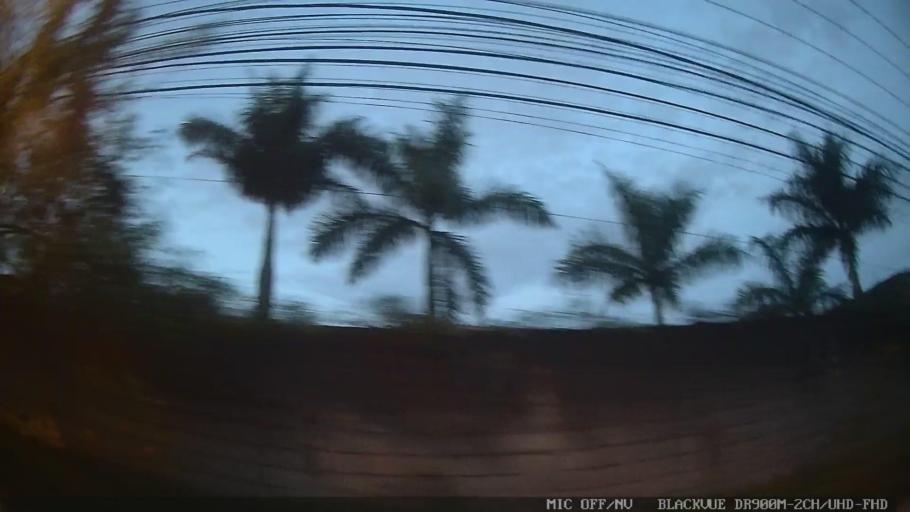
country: BR
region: Sao Paulo
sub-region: Itaquaquecetuba
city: Itaquaquecetuba
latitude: -23.4551
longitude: -46.3718
